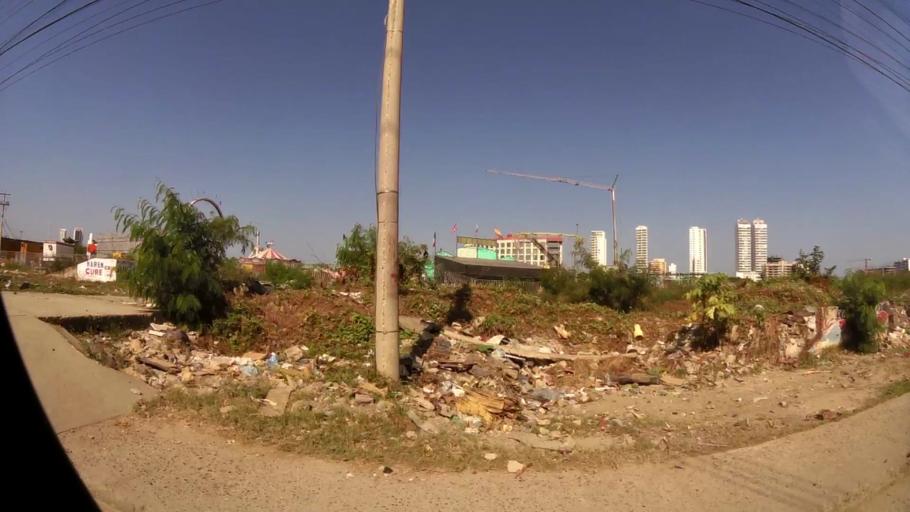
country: CO
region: Bolivar
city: Cartagena
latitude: 10.4279
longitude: -75.5381
